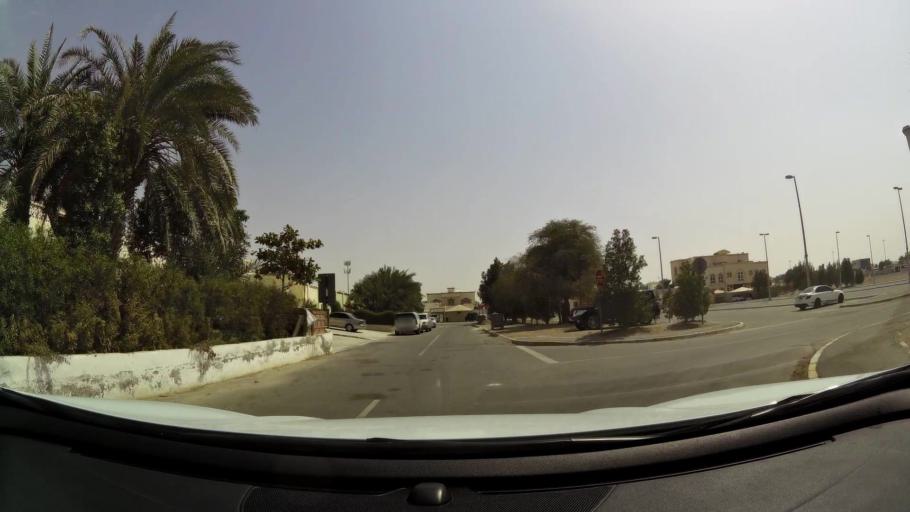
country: AE
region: Abu Dhabi
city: Abu Dhabi
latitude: 24.2935
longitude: 54.6467
